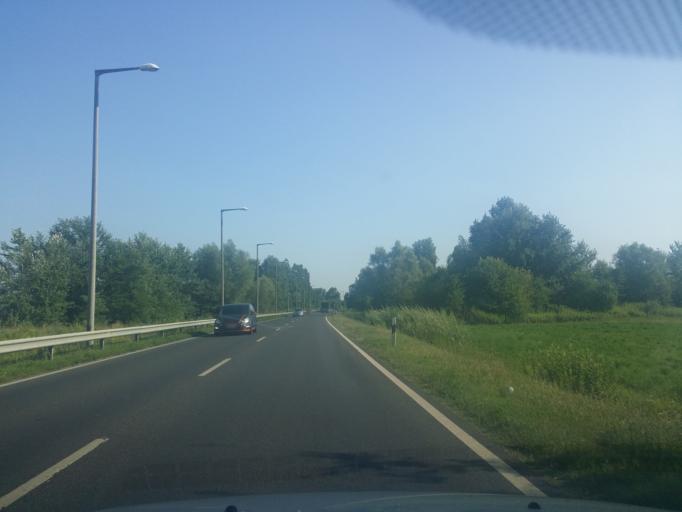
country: HU
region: Bacs-Kiskun
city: Baja
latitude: 46.1863
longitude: 18.9770
